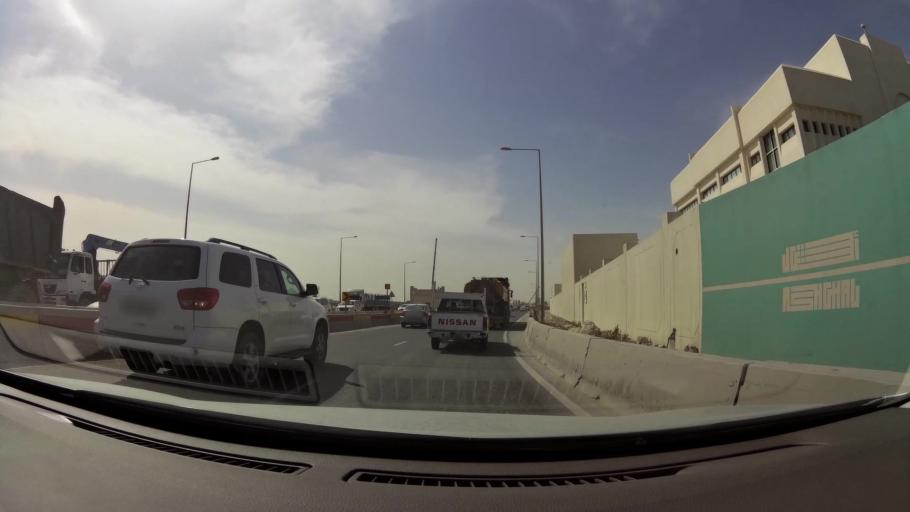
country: QA
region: Baladiyat ar Rayyan
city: Ar Rayyan
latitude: 25.3069
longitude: 51.4116
